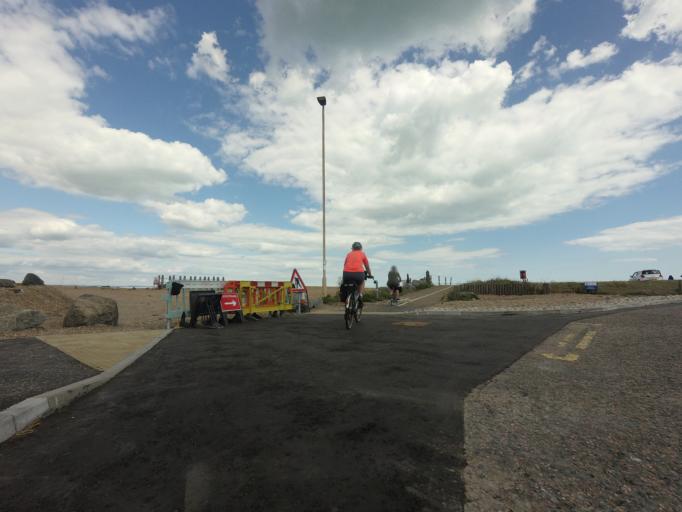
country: GB
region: England
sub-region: East Sussex
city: Pevensey
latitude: 50.7855
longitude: 0.3281
